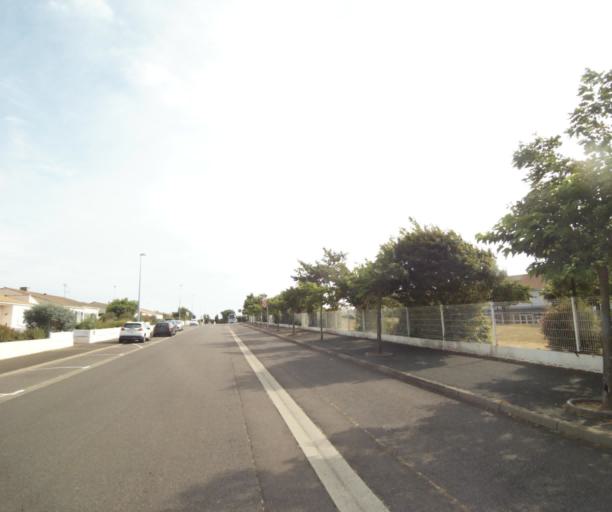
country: FR
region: Pays de la Loire
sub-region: Departement de la Vendee
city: Chateau-d'Olonne
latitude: 46.4904
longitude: -1.7438
